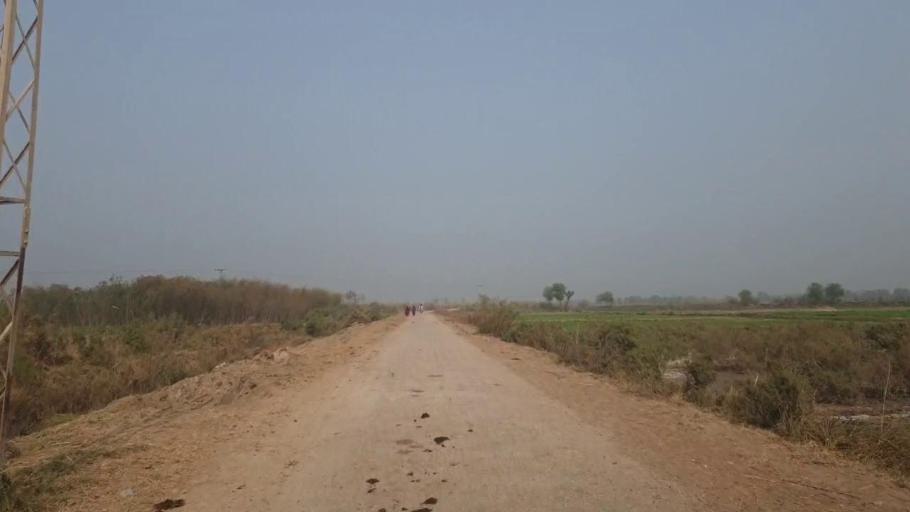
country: PK
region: Sindh
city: Bhit Shah
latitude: 25.8048
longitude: 68.5416
